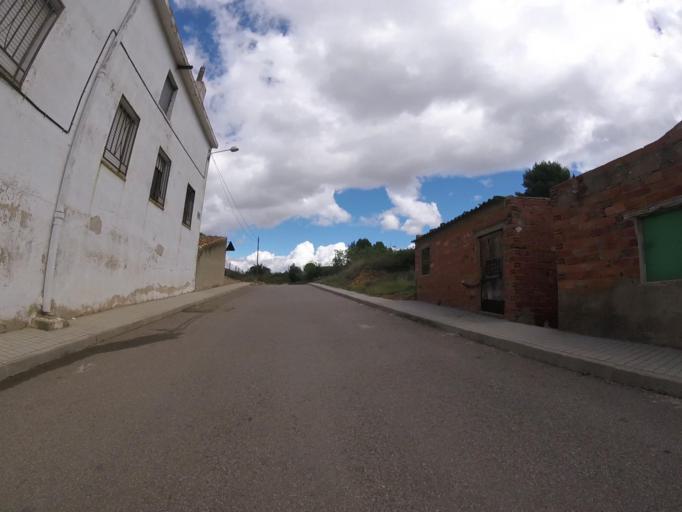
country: ES
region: Valencia
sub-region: Provincia de Castello
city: Sierra-Engarceran
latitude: 40.2934
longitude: -0.0459
